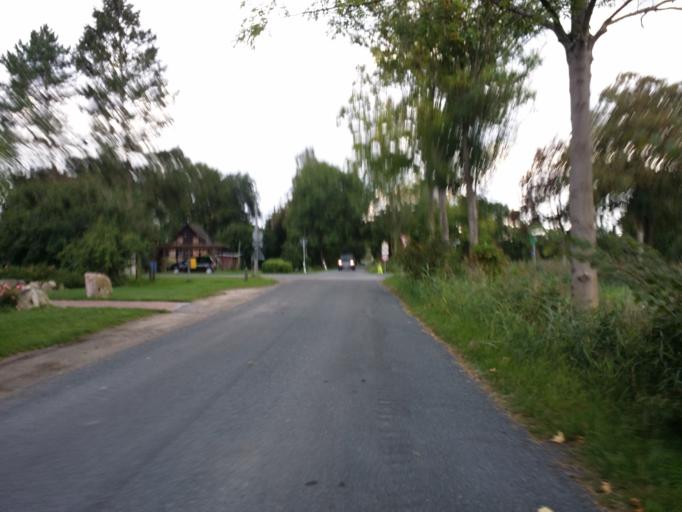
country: DE
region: Lower Saxony
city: Hemmoor
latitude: 53.7176
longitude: 9.1703
